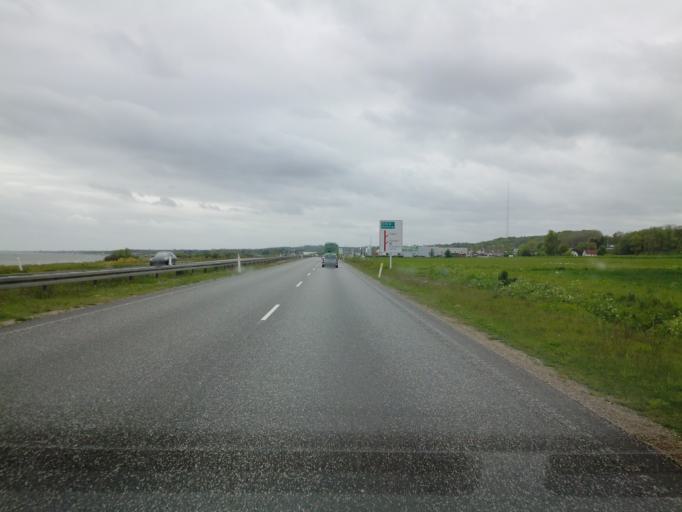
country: DK
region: North Denmark
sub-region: Frederikshavn Kommune
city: Frederikshavn
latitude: 57.3951
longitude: 10.5165
